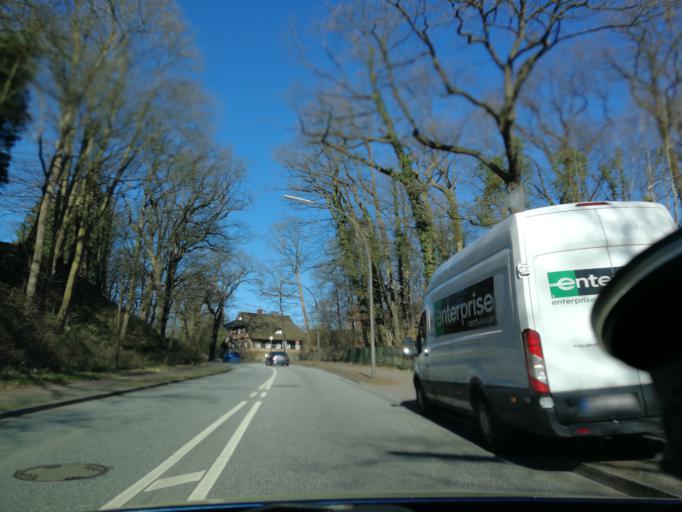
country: DE
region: Hamburg
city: Harburg
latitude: 53.4537
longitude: 9.9548
